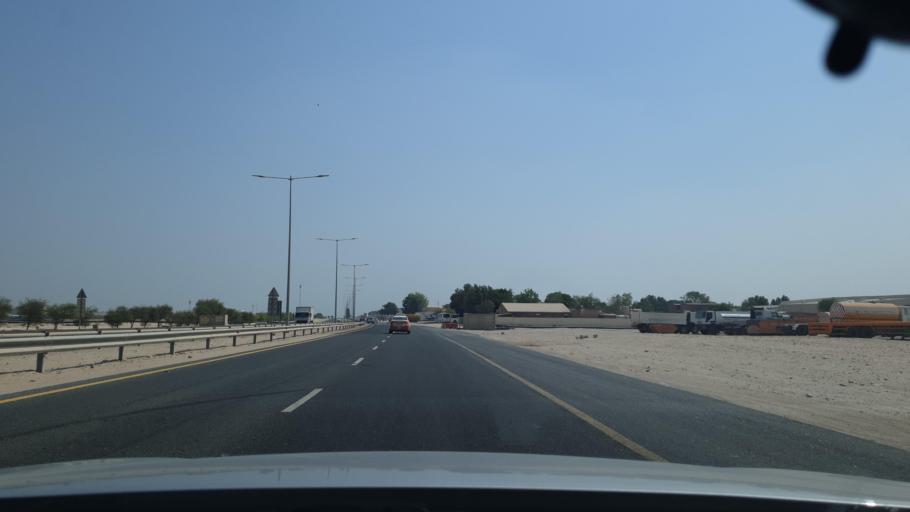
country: QA
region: Al Khawr
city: Al Khawr
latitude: 25.7200
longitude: 51.5008
